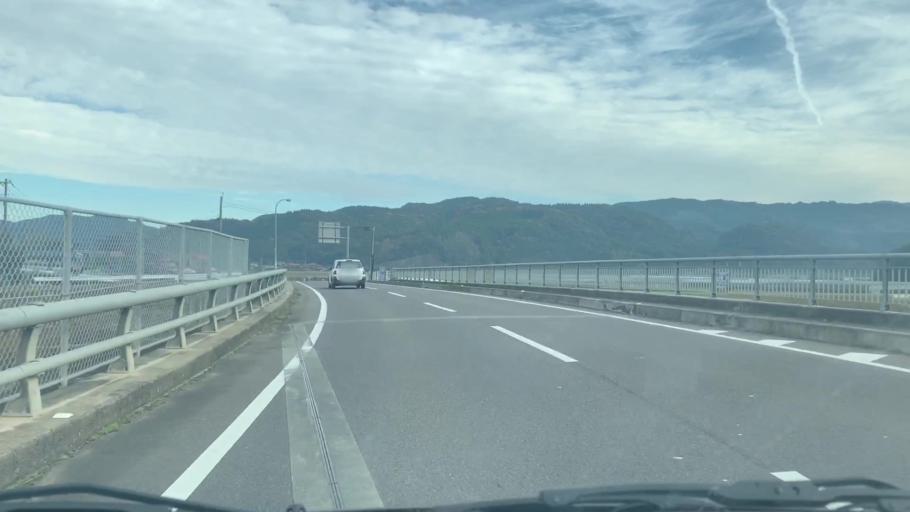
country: JP
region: Saga Prefecture
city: Imaricho-ko
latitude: 33.3084
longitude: 129.9703
